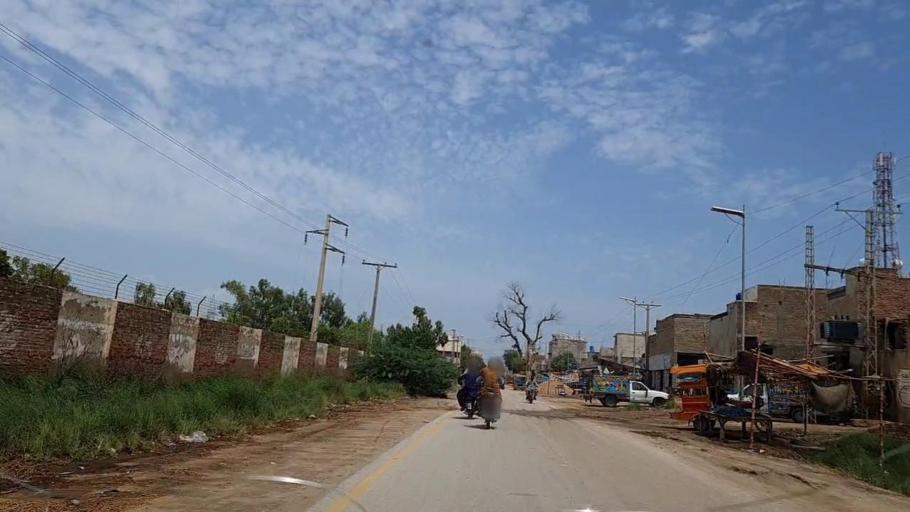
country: PK
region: Sindh
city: Naushahro Firoz
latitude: 26.8428
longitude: 68.1119
